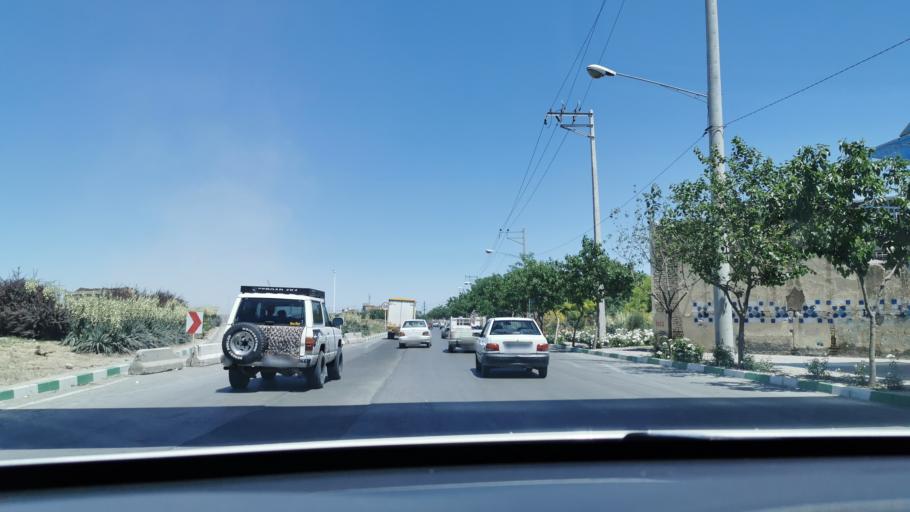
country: IR
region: Razavi Khorasan
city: Mashhad
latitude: 36.2589
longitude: 59.6432
